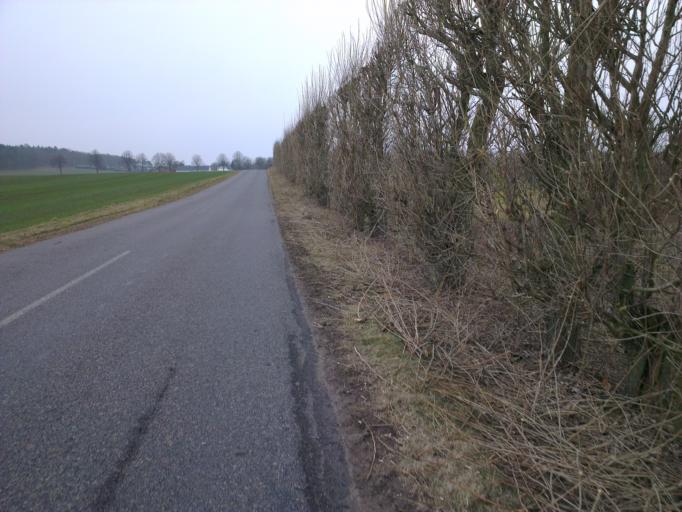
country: DK
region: Capital Region
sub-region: Frederikssund Kommune
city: Skibby
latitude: 55.7924
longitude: 11.9675
